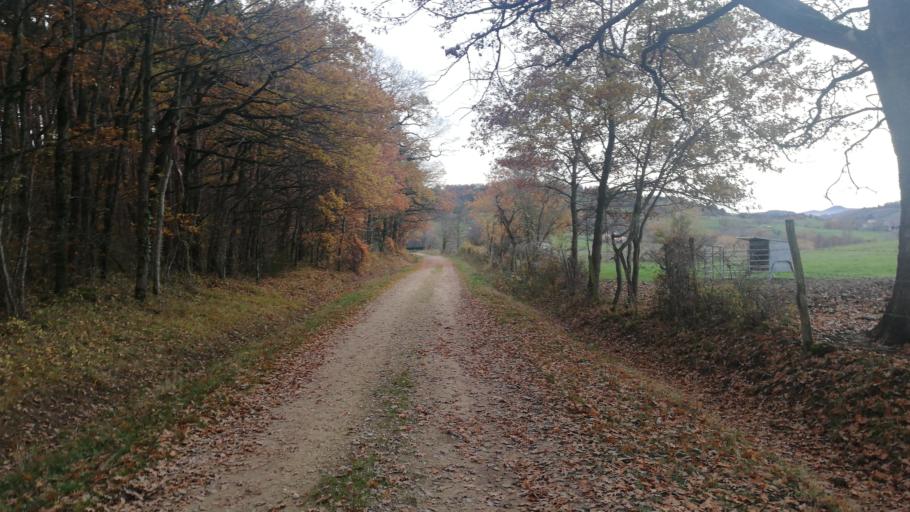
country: FR
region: Auvergne
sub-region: Departement du Puy-de-Dome
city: Billom
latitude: 45.6934
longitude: 3.3687
